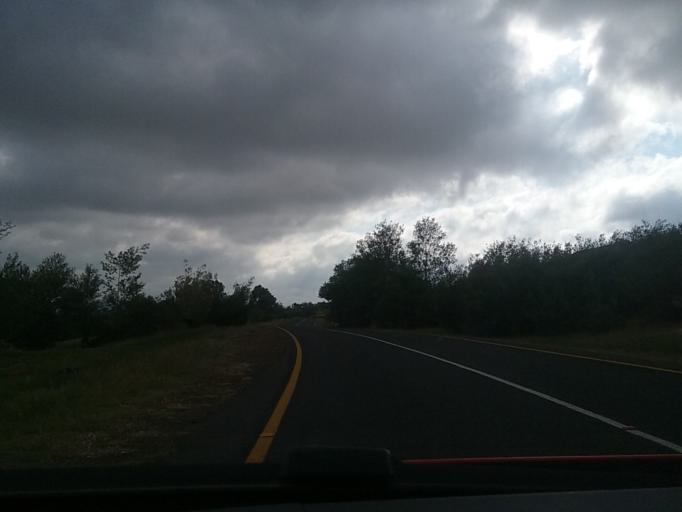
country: LS
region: Berea
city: Teyateyaneng
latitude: -29.1839
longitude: 27.7926
